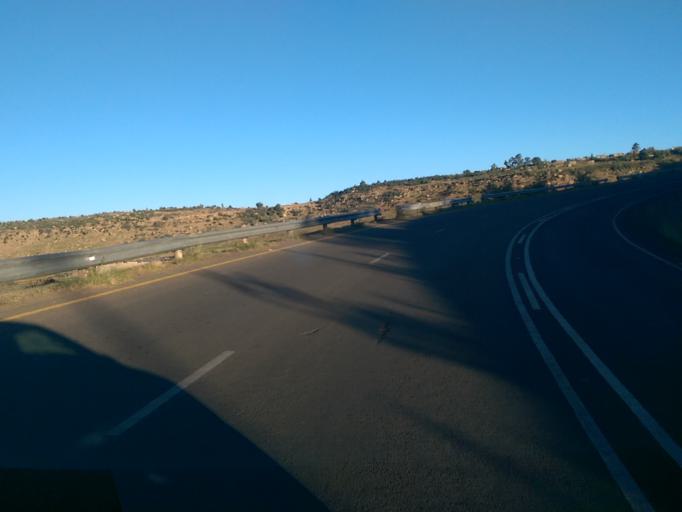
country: LS
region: Maseru
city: Maseru
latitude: -29.4022
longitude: 27.5737
